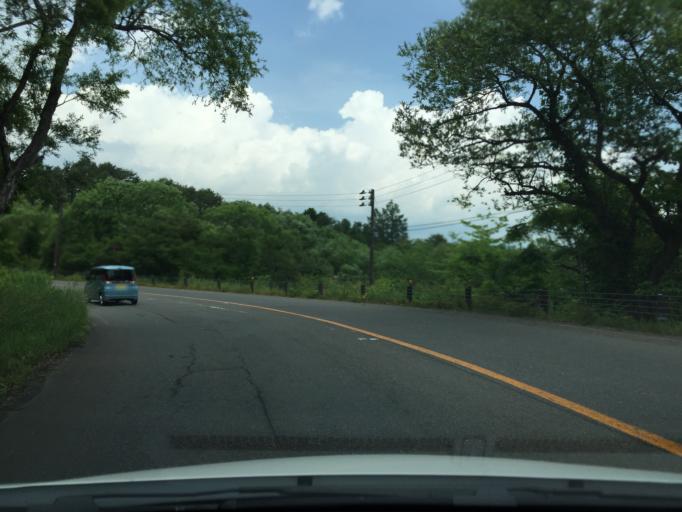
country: JP
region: Fukushima
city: Inawashiro
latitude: 37.6470
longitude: 140.1018
